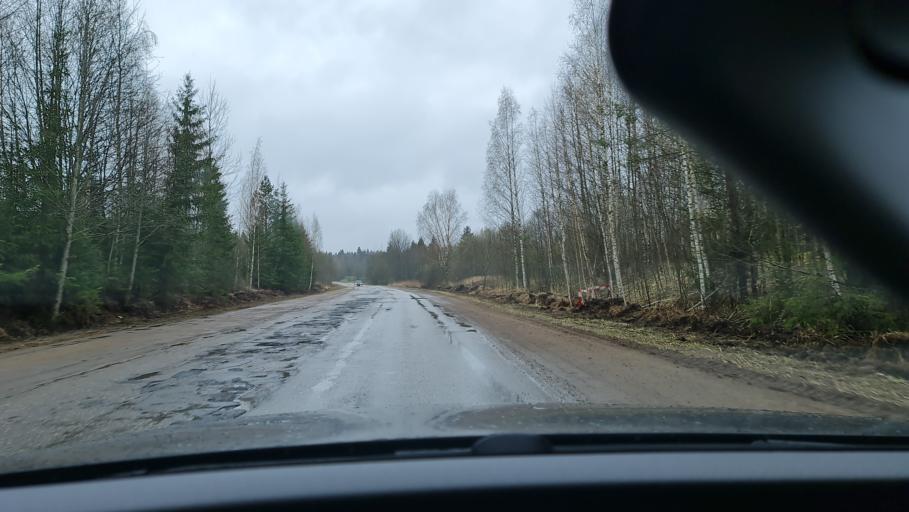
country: RU
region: Novgorod
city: Kresttsy
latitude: 58.0343
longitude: 32.8332
